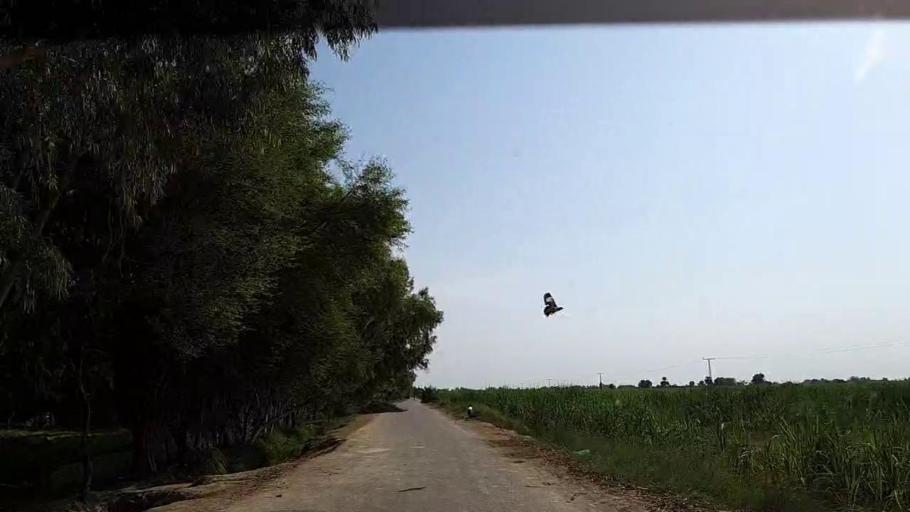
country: PK
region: Sindh
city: Adilpur
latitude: 27.9305
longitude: 69.2541
